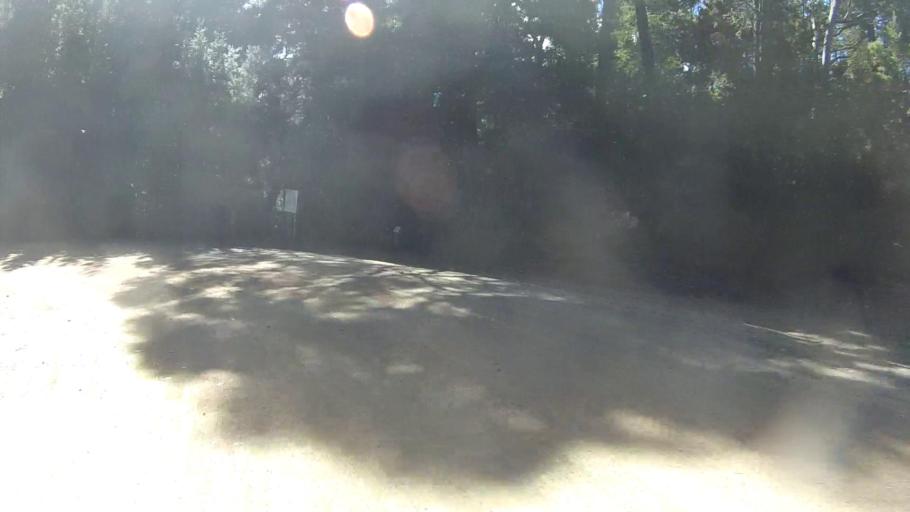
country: AU
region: Tasmania
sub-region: Derwent Valley
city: New Norfolk
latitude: -42.6820
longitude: 146.6747
